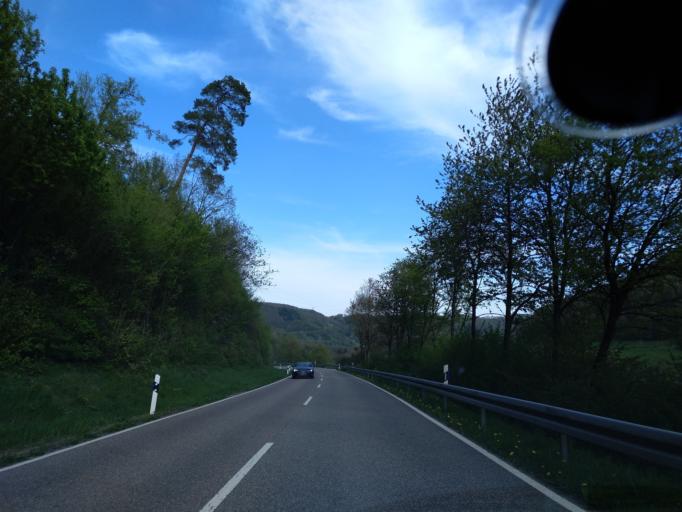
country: DE
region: Baden-Wuerttemberg
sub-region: Regierungsbezirk Stuttgart
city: Braunsbach
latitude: 49.2226
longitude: 9.7515
